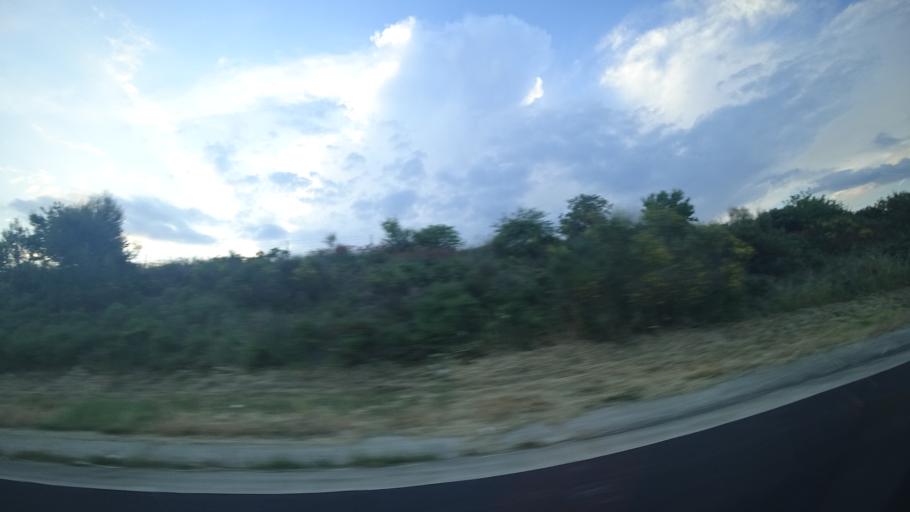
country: FR
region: Languedoc-Roussillon
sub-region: Departement de l'Herault
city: Paulhan
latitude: 43.5490
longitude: 3.4500
